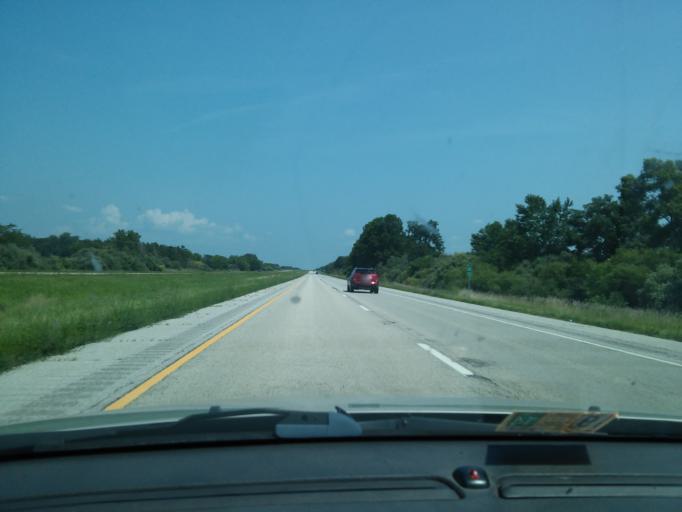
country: US
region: Illinois
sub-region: Sangamon County
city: New Berlin
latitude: 39.7398
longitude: -89.9637
